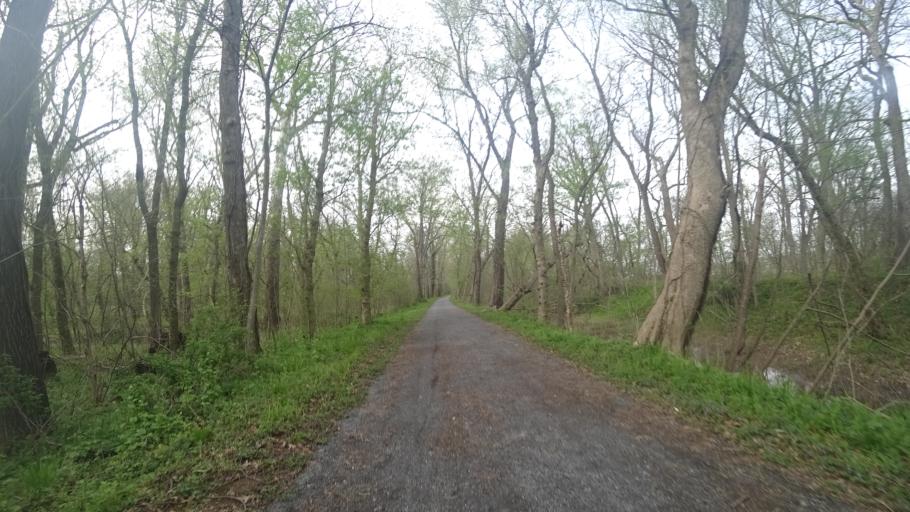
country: US
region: Virginia
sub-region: Loudoun County
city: Leesburg
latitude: 39.1480
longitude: -77.5180
